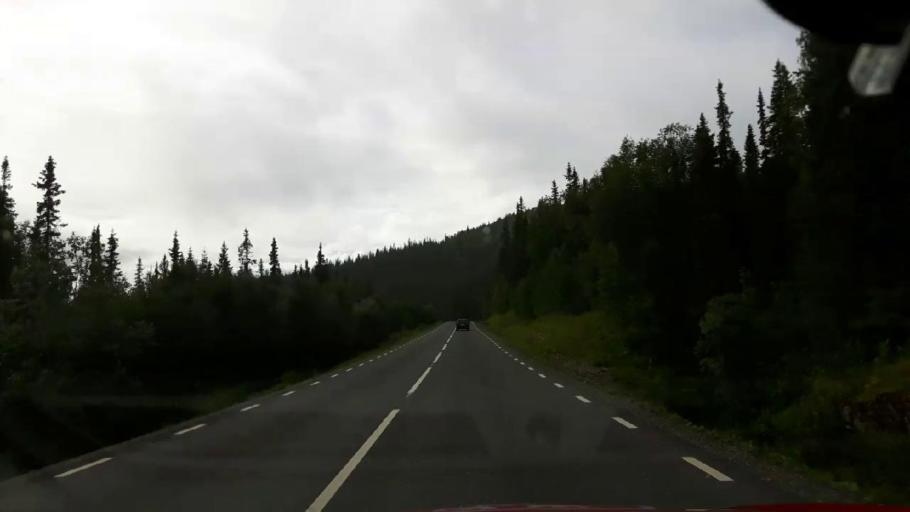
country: NO
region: Nord-Trondelag
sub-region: Royrvik
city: Royrvik
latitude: 64.8629
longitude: 14.1865
